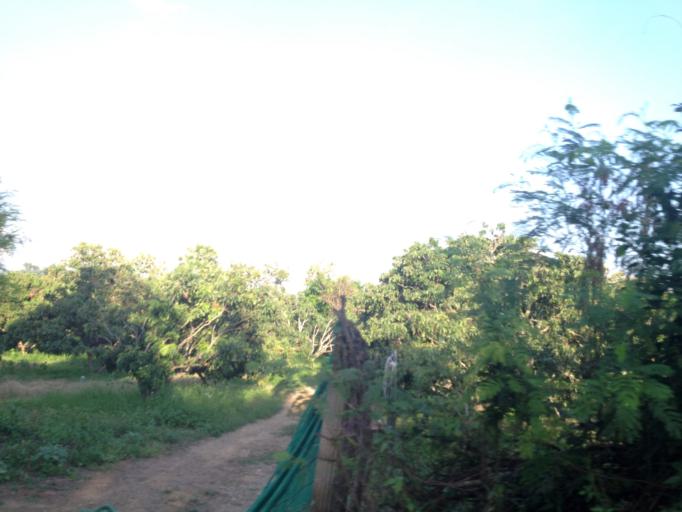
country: TH
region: Chiang Mai
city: Hang Dong
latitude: 18.7229
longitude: 98.9055
